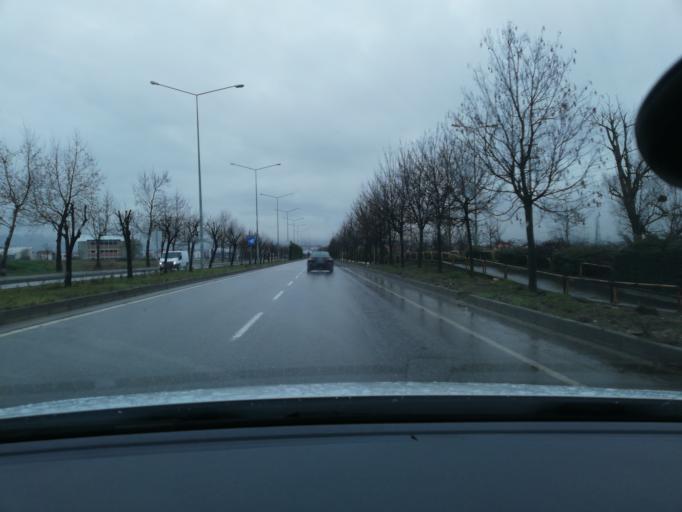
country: TR
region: Bolu
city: Bolu
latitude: 40.7153
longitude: 31.6150
